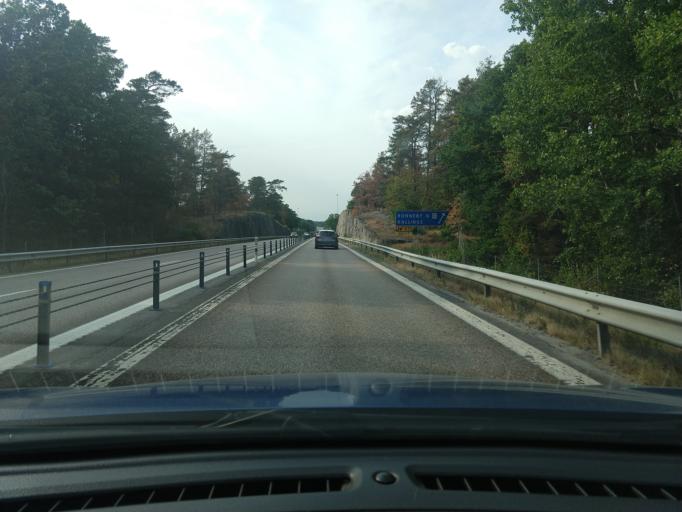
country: SE
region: Blekinge
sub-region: Ronneby Kommun
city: Ronneby
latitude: 56.2186
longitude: 15.2869
